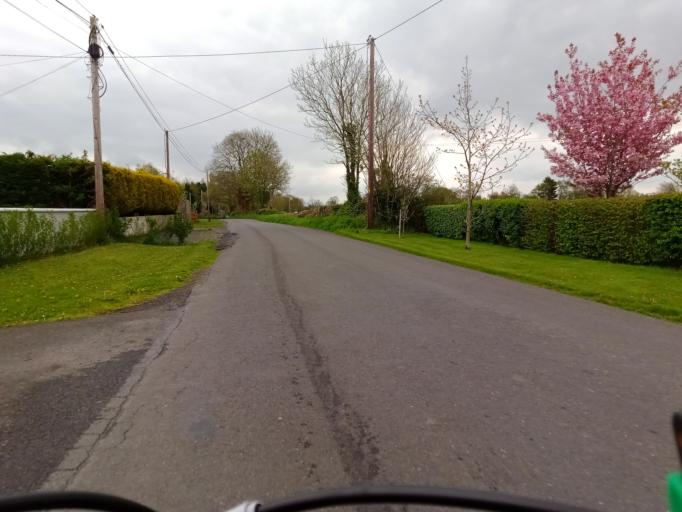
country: IE
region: Leinster
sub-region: Kilkenny
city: Kilkenny
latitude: 52.6205
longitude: -7.2781
